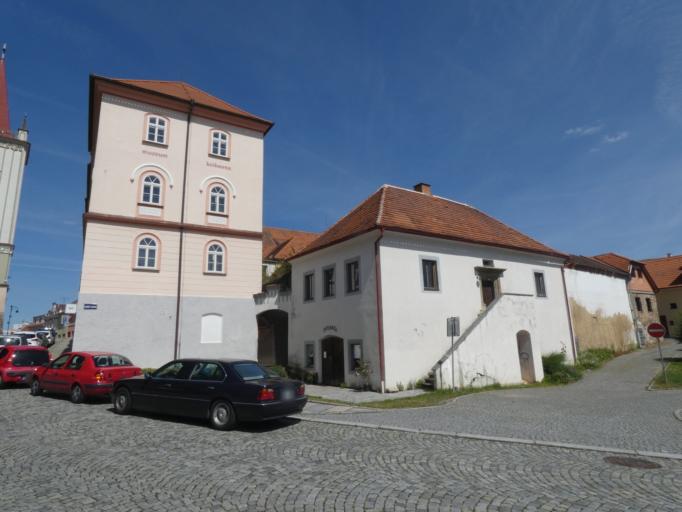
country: CZ
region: Jihocesky
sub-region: Okres Strakonice
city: Blatna
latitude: 49.4242
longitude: 13.8813
